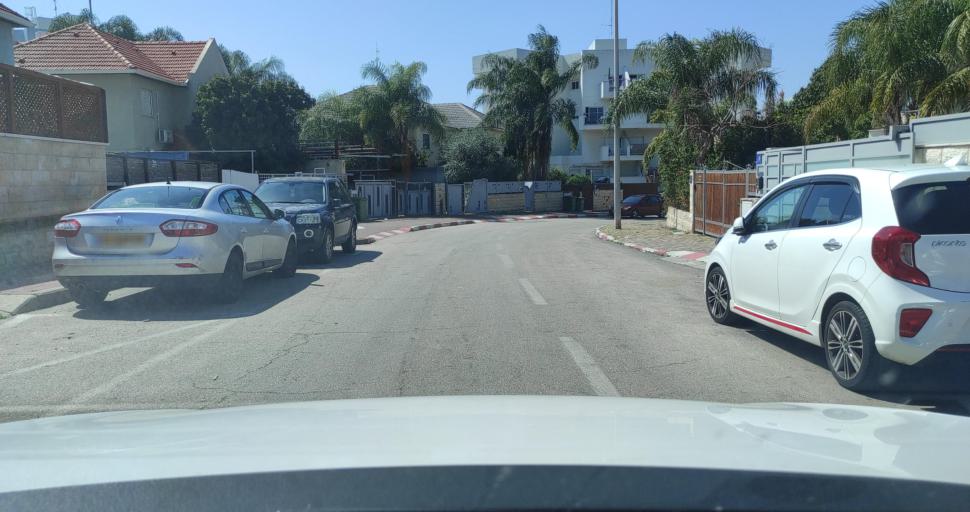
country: IL
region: Central District
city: Nordiyya
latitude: 32.3075
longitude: 34.8821
